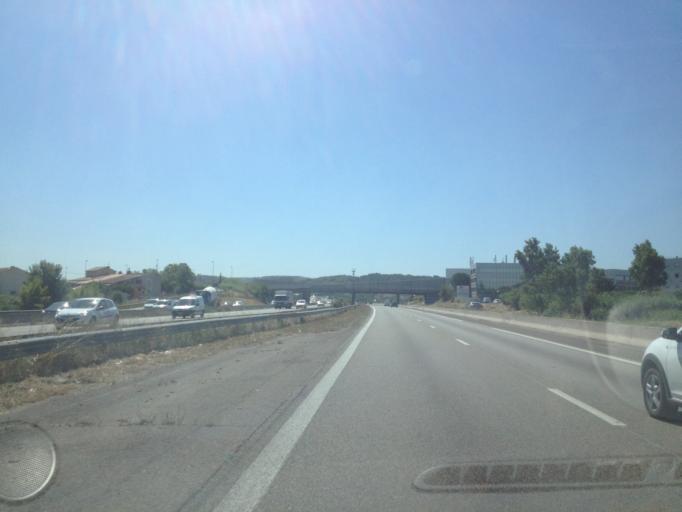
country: FR
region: Provence-Alpes-Cote d'Azur
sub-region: Departement des Bouches-du-Rhone
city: Saint-Victoret
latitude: 43.4232
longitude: 5.2666
